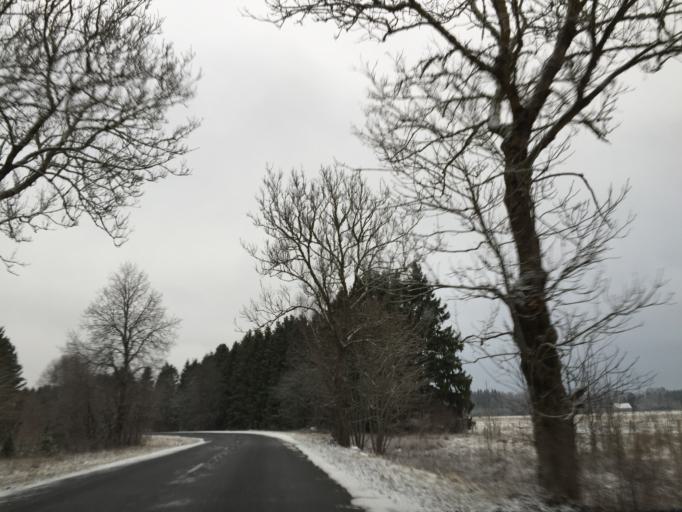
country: EE
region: Saare
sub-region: Orissaare vald
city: Orissaare
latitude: 58.6077
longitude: 23.3094
